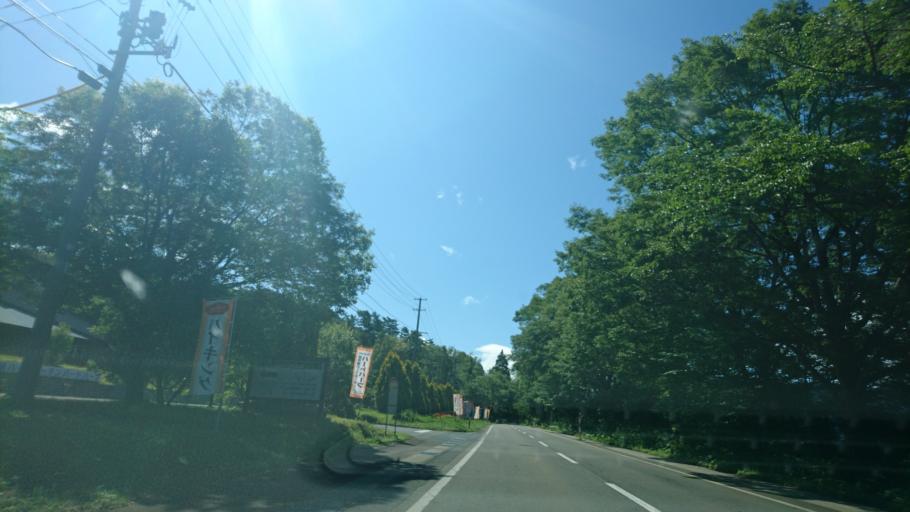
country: JP
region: Akita
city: Kakunodatemachi
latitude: 39.7433
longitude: 140.6859
